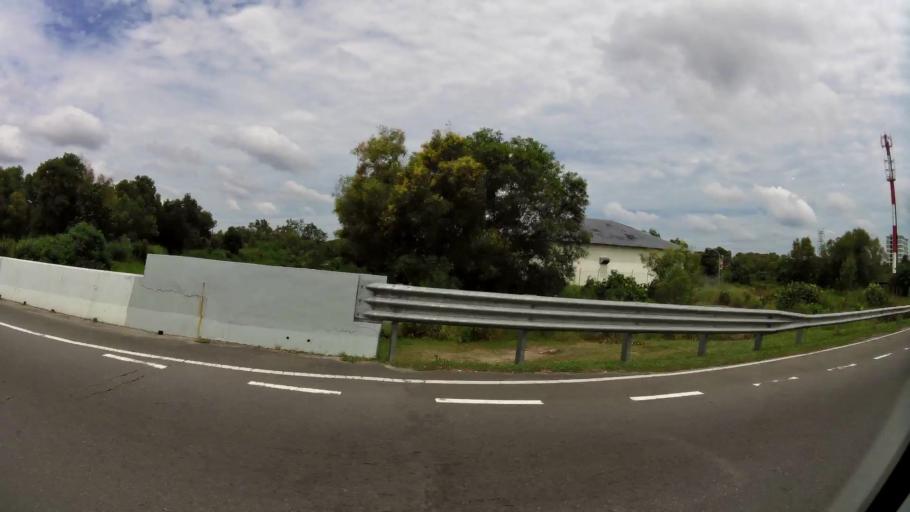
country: BN
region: Brunei and Muara
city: Bandar Seri Begawan
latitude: 4.9240
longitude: 114.9221
